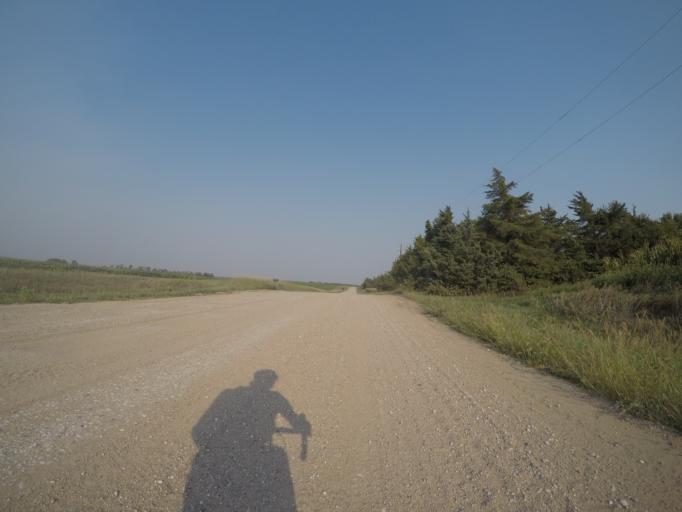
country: US
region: Nebraska
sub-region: Gage County
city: Beatrice
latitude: 40.2629
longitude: -96.8130
